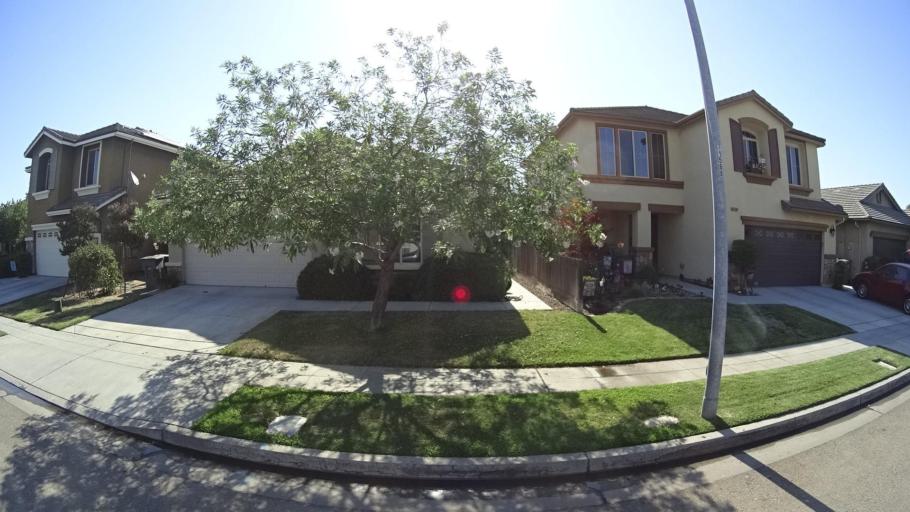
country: US
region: California
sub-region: Fresno County
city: Tarpey Village
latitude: 36.7823
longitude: -119.6558
